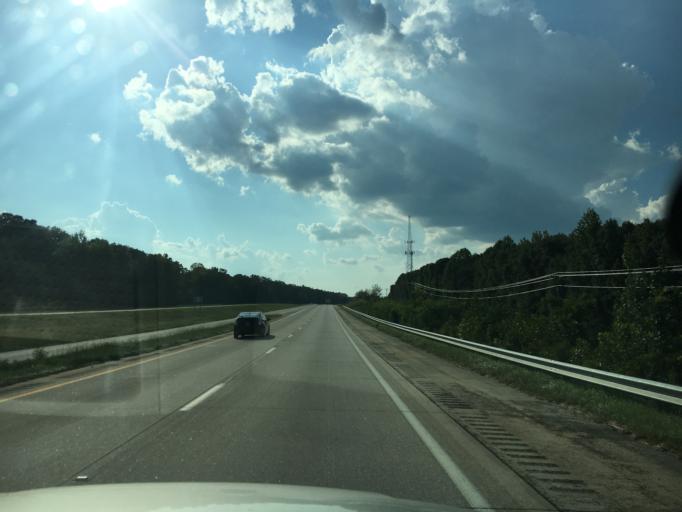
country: US
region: South Carolina
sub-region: Laurens County
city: Watts Mills
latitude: 34.5437
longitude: -81.9716
